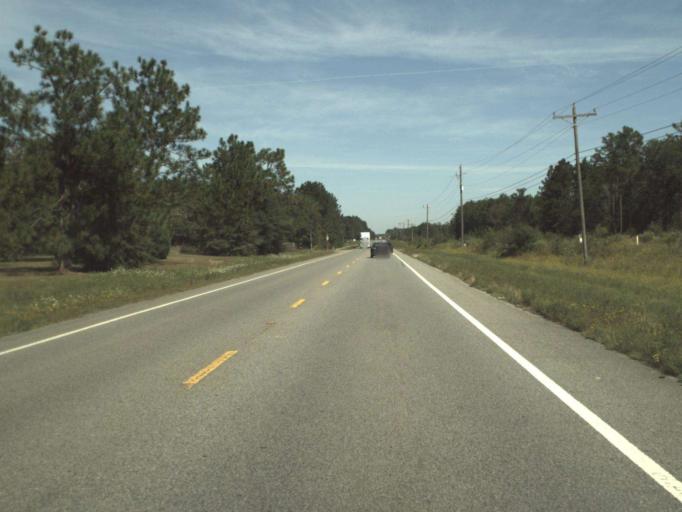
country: US
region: Florida
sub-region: Bay County
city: Lynn Haven
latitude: 30.4804
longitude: -85.6642
